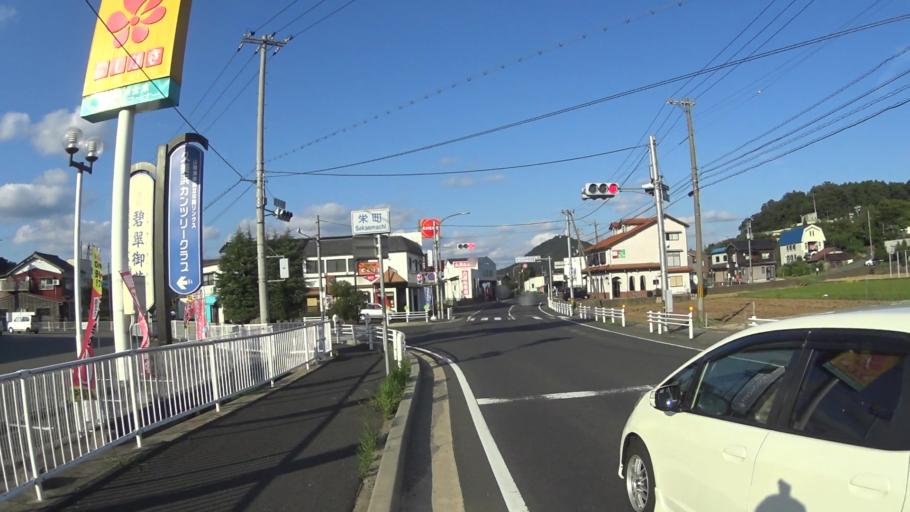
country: JP
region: Hyogo
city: Toyooka
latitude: 35.5979
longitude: 134.8895
